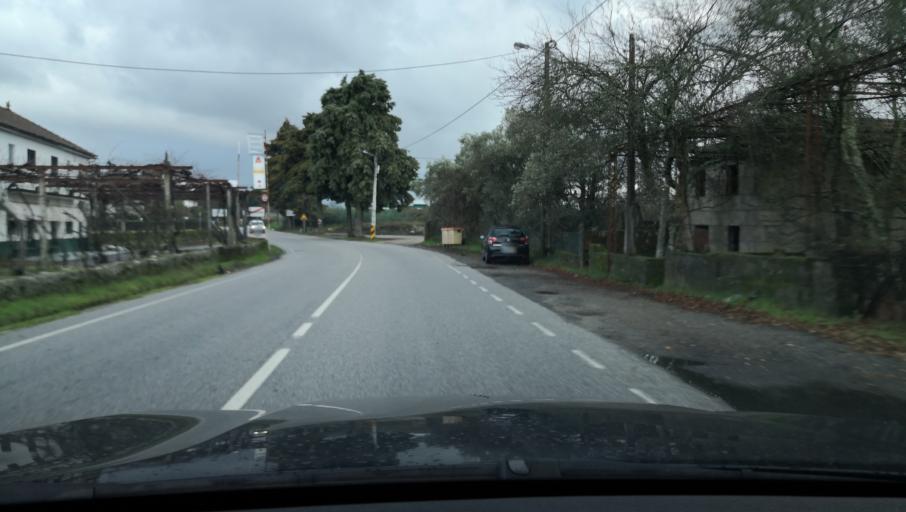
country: PT
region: Vila Real
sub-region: Vila Real
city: Vila Real
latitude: 41.3251
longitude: -7.7287
